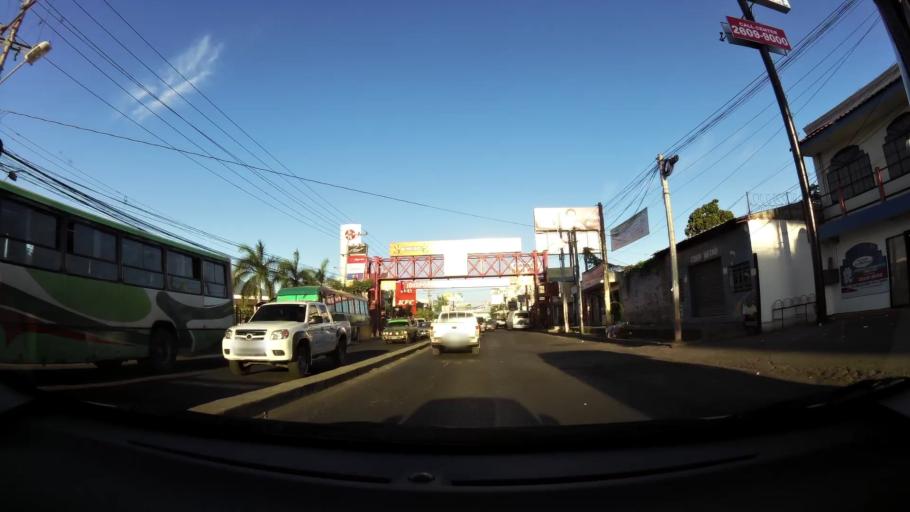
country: SV
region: San Miguel
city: San Miguel
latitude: 13.4624
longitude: -88.1651
